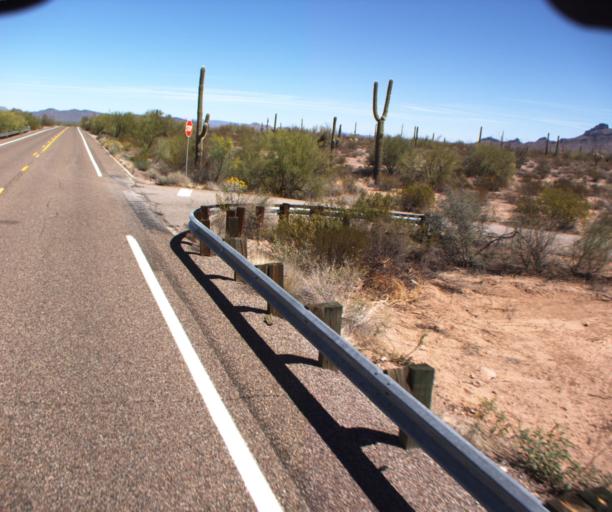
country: MX
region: Sonora
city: Sonoyta
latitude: 32.0912
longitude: -112.7748
